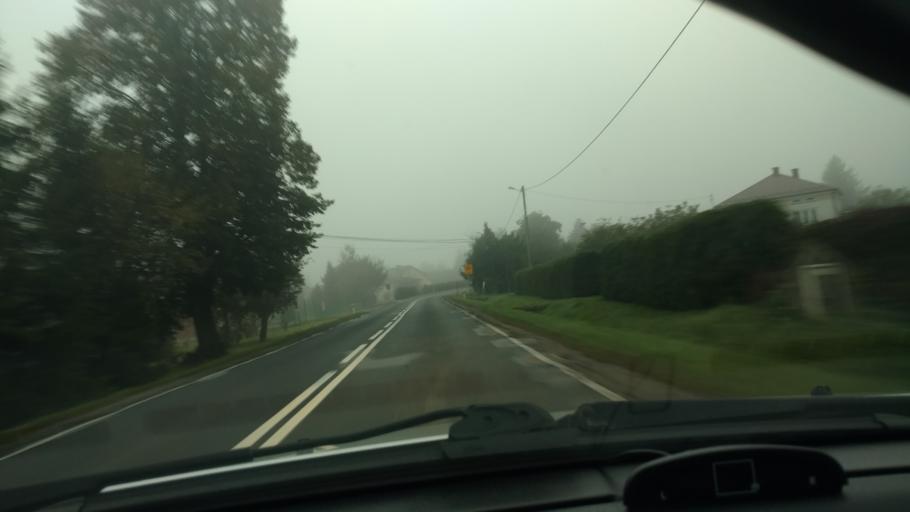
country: PL
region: Subcarpathian Voivodeship
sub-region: Powiat strzyzowski
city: Wisniowa
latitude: 49.8718
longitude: 21.6867
